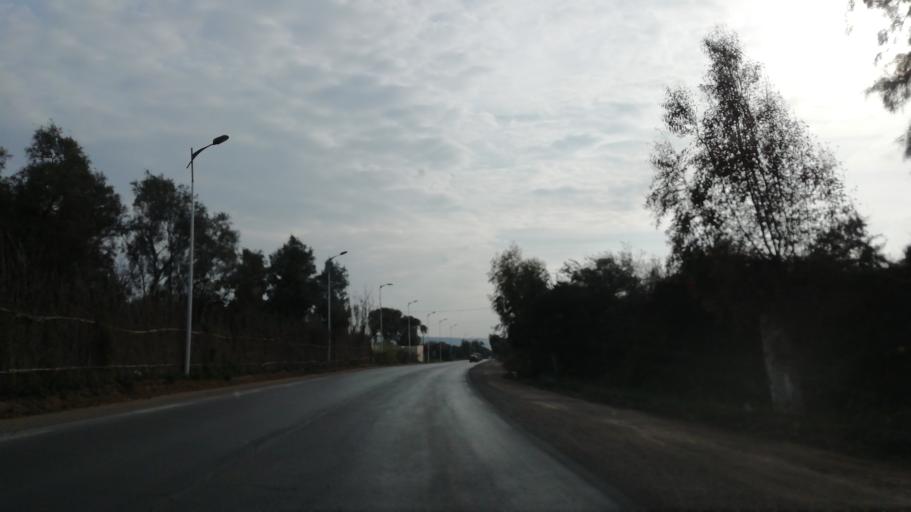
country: DZ
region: Mostaganem
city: Mostaganem
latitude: 35.8785
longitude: 0.0789
